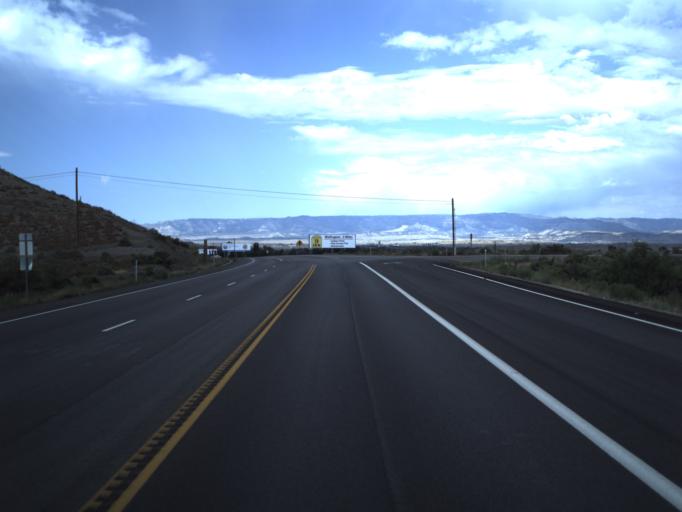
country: US
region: Utah
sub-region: Carbon County
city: Wellington
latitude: 39.5494
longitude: -110.6671
